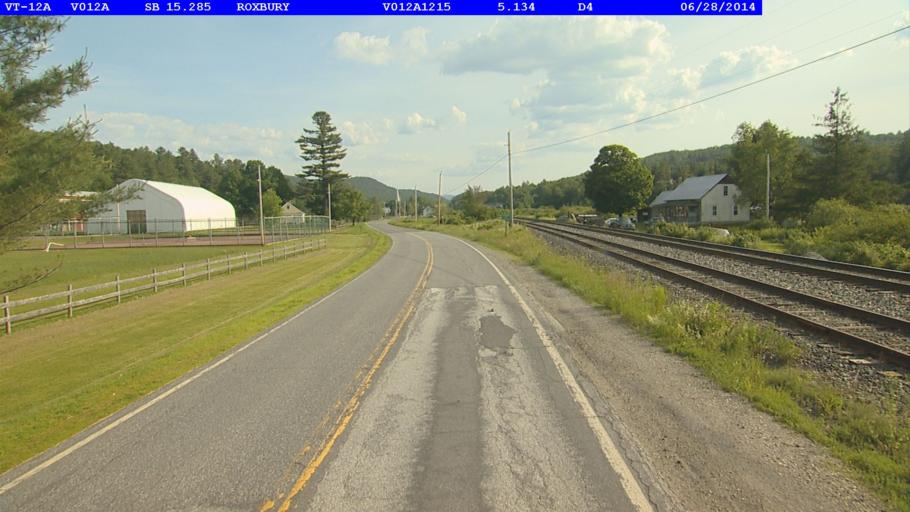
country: US
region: Vermont
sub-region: Washington County
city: Northfield
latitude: 44.0993
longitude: -72.7317
